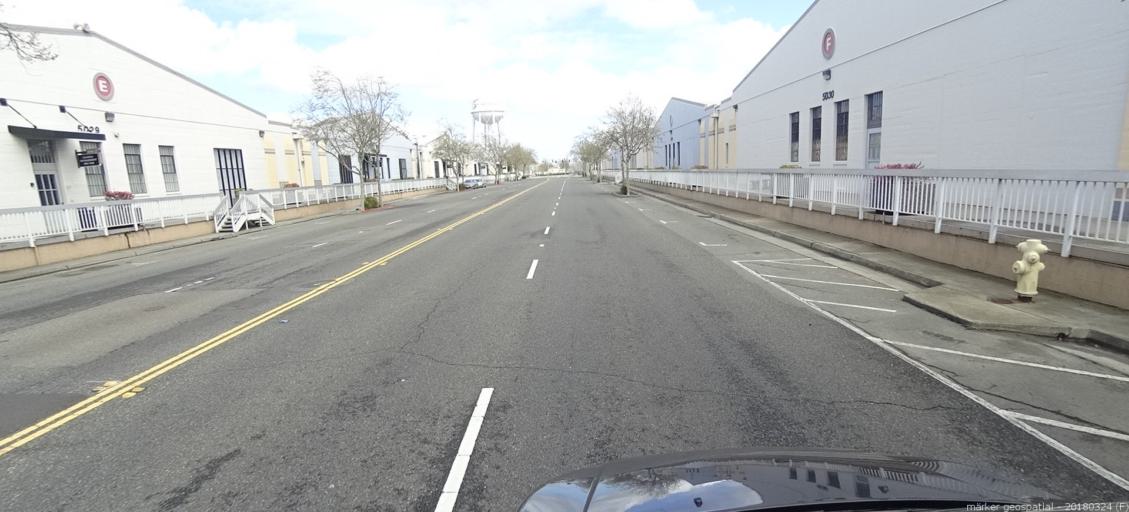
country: US
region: California
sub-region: Sacramento County
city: North Highlands
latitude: 38.6585
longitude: -121.3881
